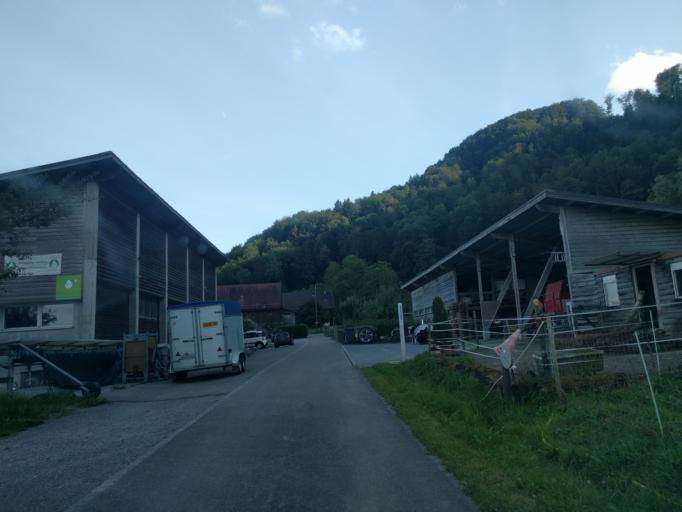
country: CH
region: Zurich
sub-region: Bezirk Zuerich
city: Zuerich (Kreis 2) / Mittel-Leimbach
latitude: 47.3245
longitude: 8.5051
